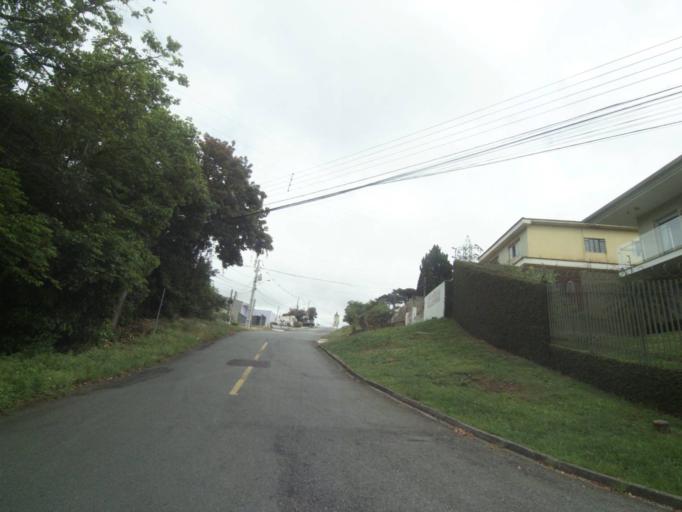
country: BR
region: Parana
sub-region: Curitiba
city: Curitiba
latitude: -25.3896
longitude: -49.2800
